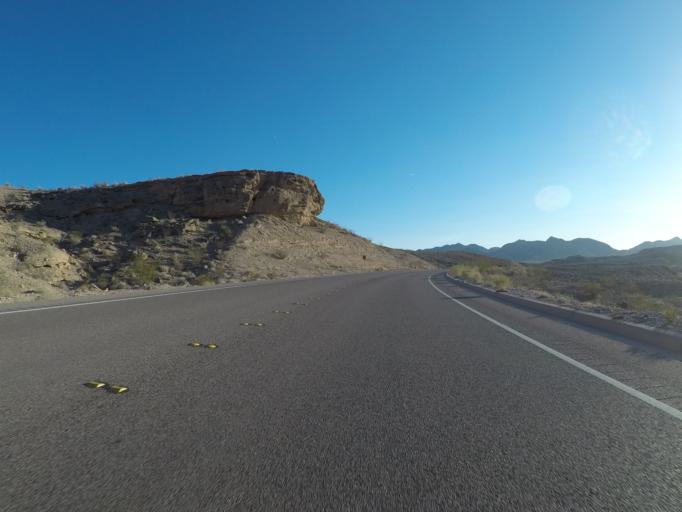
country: US
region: Nevada
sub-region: Clark County
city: Moapa Valley
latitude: 36.3023
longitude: -114.4890
